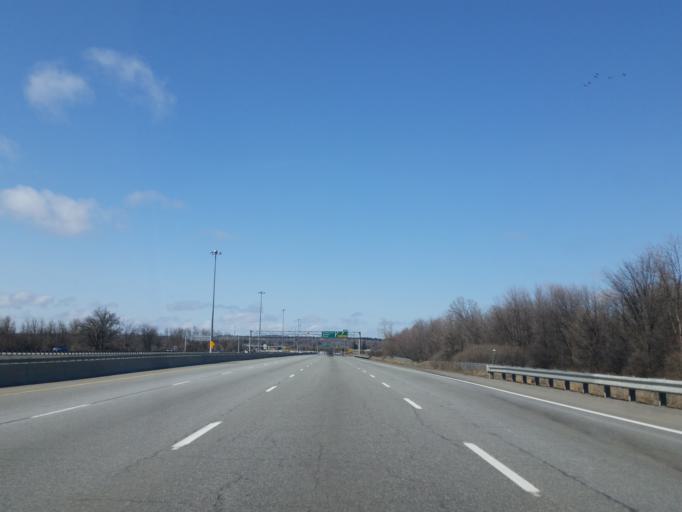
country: CA
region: Ontario
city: Bells Corners
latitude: 45.3427
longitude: -75.8264
